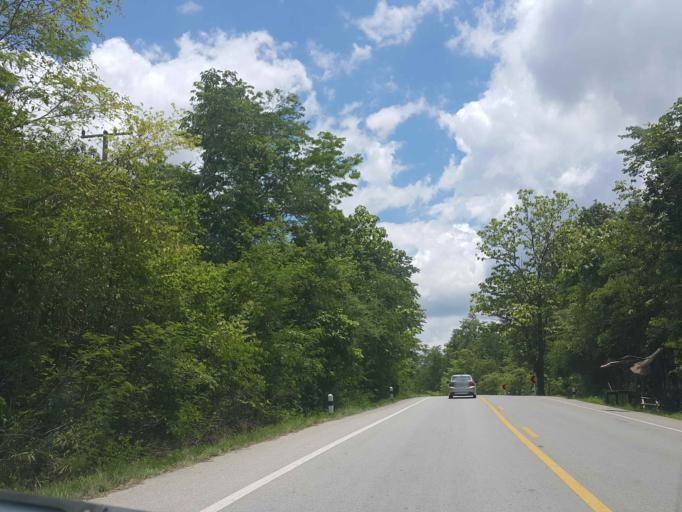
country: TH
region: Nan
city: Wiang Sa
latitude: 18.5201
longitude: 100.6063
